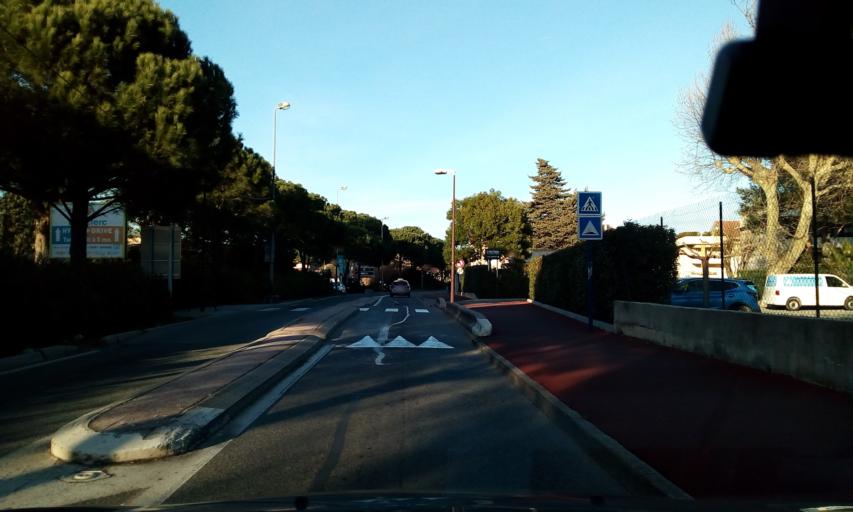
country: FR
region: Provence-Alpes-Cote d'Azur
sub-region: Departement du Var
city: Frejus
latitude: 43.4256
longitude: 6.7332
